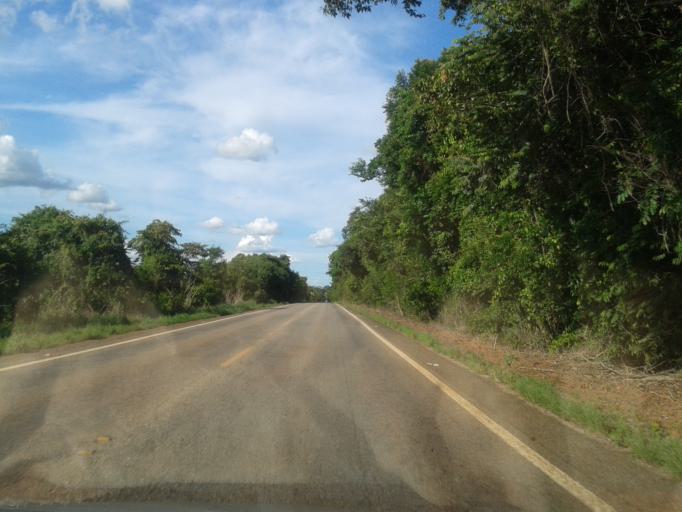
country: BR
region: Goias
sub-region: Mozarlandia
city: Mozarlandia
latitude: -14.4377
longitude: -50.4573
